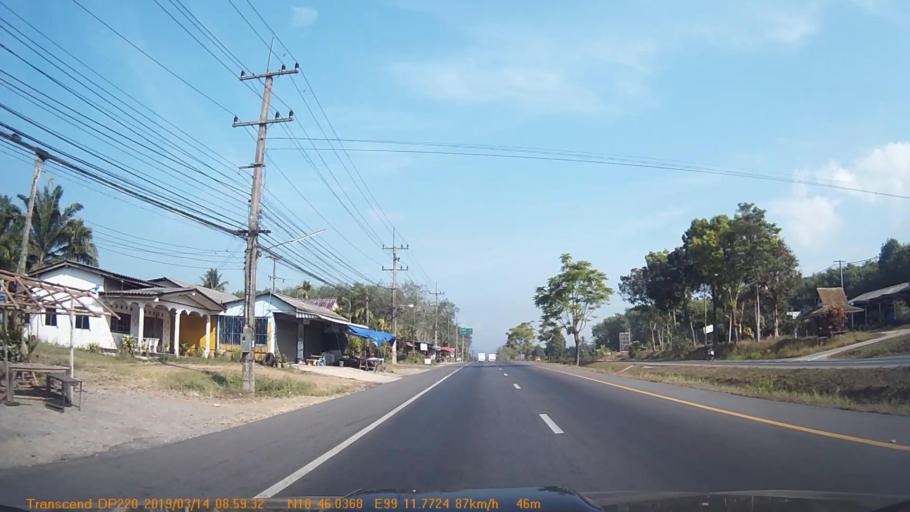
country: TH
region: Chumphon
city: Tha Sae
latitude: 10.7675
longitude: 99.1961
